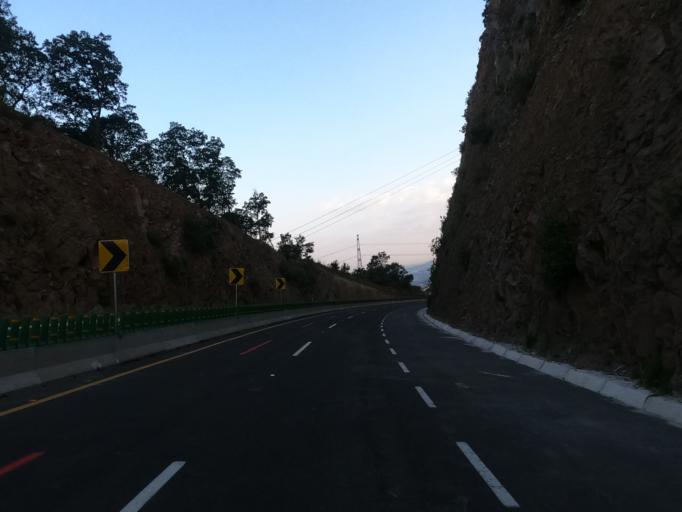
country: MX
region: Mexico
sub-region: Naucalpan de Juarez
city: Llano de las Flores (Barrio del Hueso)
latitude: 19.4336
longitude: -99.3318
